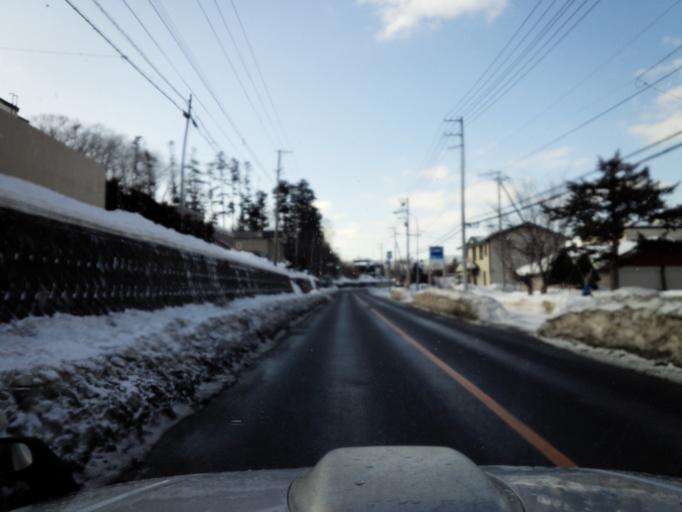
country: JP
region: Hokkaido
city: Sapporo
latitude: 42.9454
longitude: 141.3466
